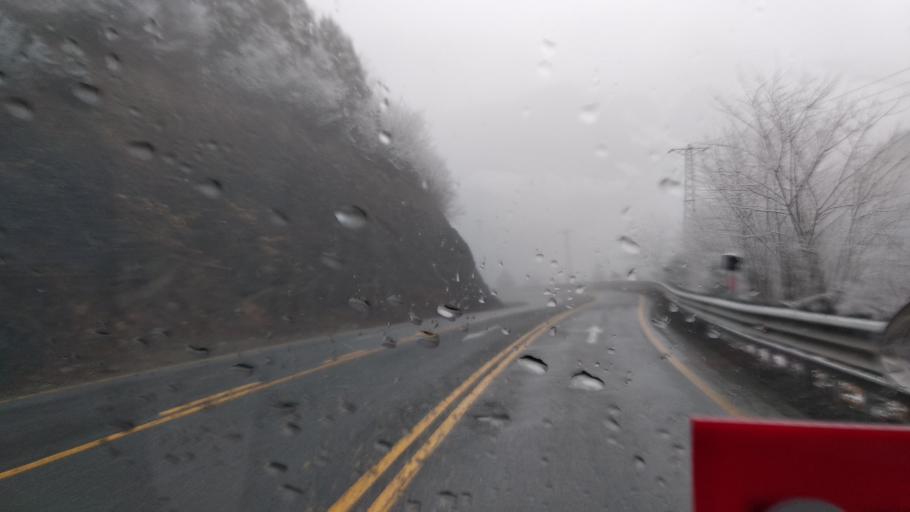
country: TR
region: Gumushane
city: Yaglidere
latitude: 40.6988
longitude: 39.4754
